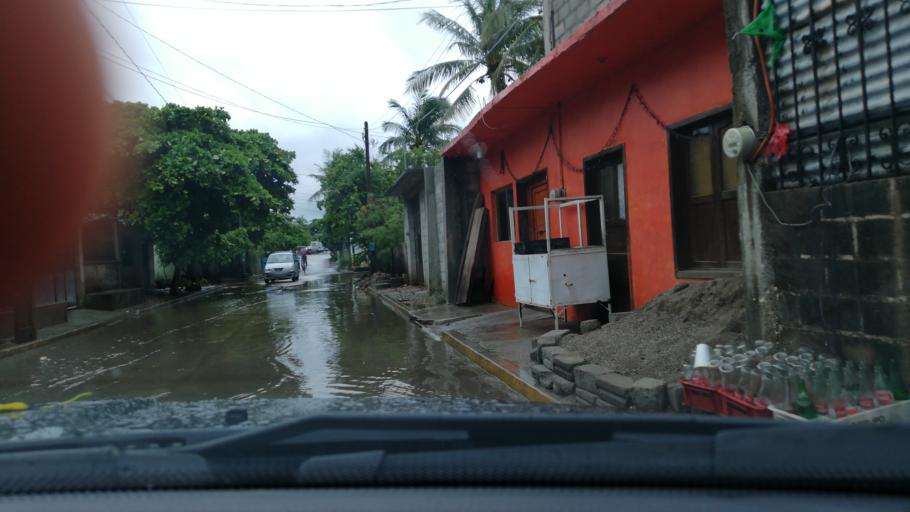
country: MX
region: Oaxaca
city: Juchitan de Zaragoza
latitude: 16.4485
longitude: -95.0188
